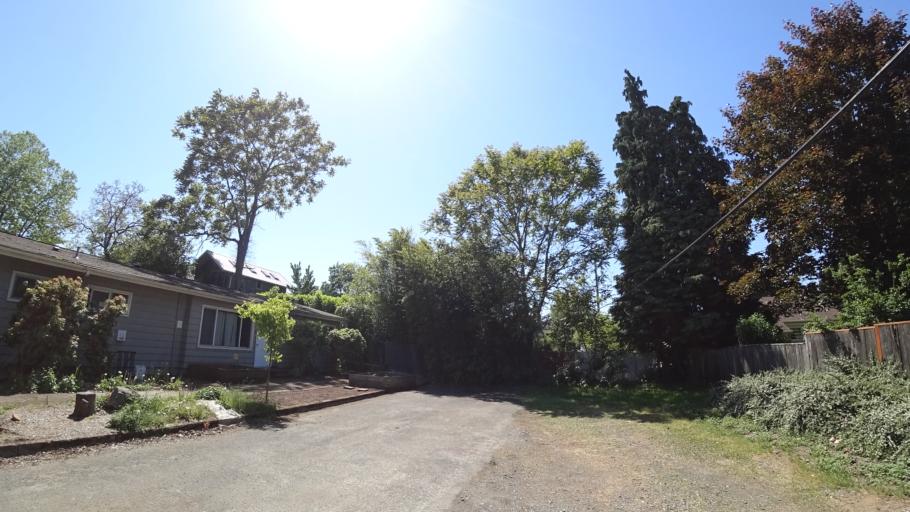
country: US
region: Oregon
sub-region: Multnomah County
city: Lents
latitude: 45.4990
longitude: -122.6064
